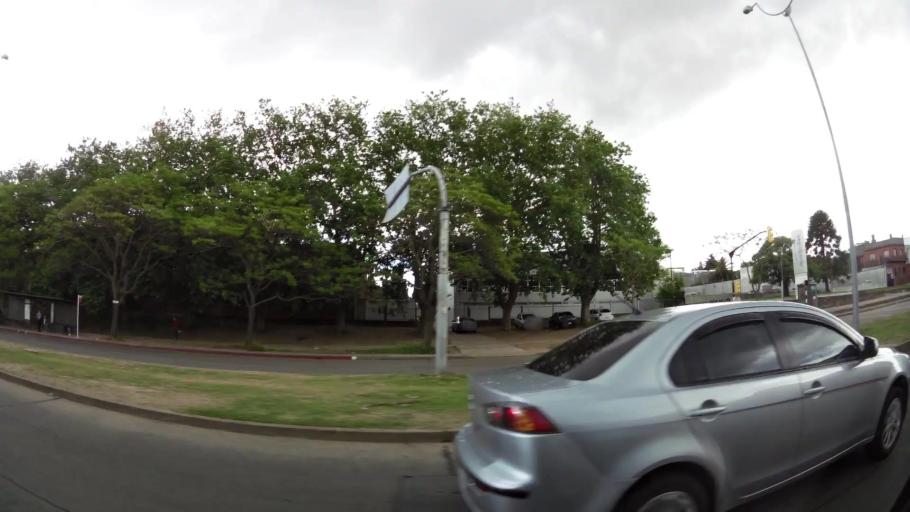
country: UY
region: Montevideo
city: Montevideo
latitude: -34.8616
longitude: -56.1679
